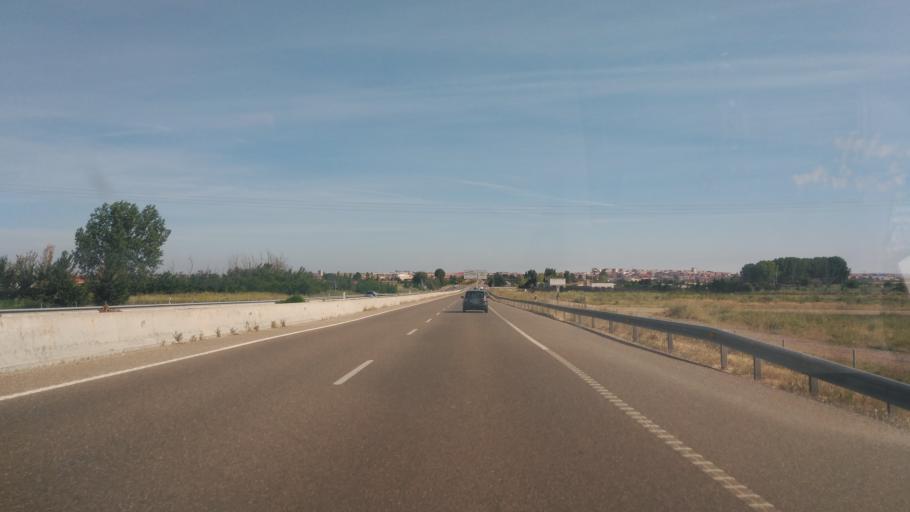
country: ES
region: Castille and Leon
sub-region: Provincia de Zamora
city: Morales del Vino
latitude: 41.4746
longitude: -5.7395
